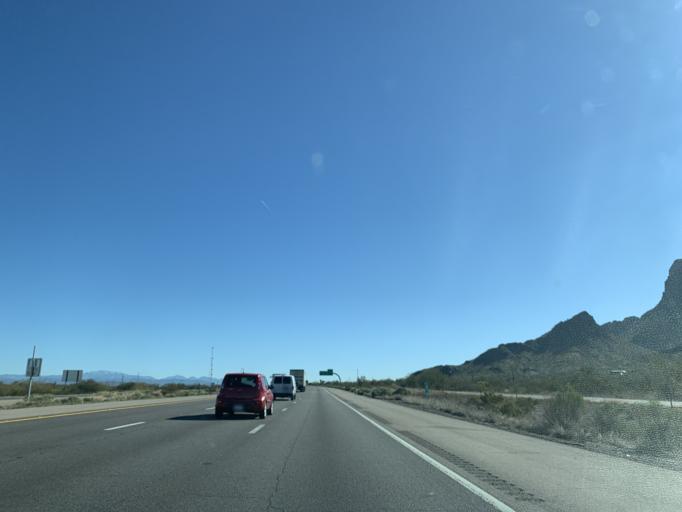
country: US
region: Arizona
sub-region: Pinal County
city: Eloy
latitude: 32.6555
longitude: -111.4051
